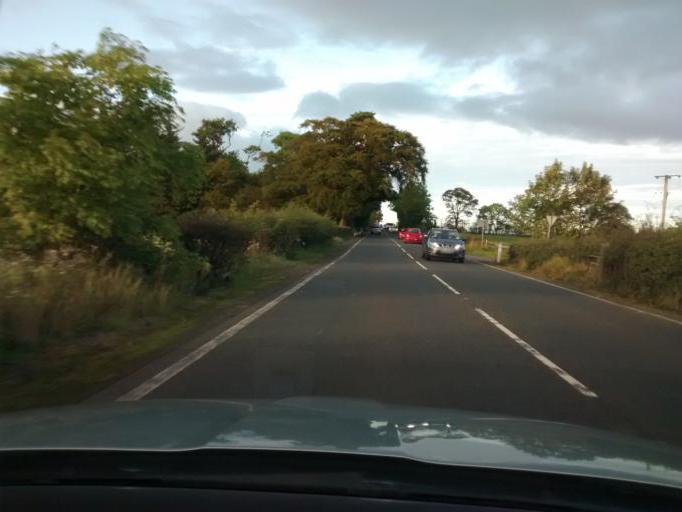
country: GB
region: Scotland
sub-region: Renfrewshire
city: Lochwinnoch
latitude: 55.7890
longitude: -4.6036
